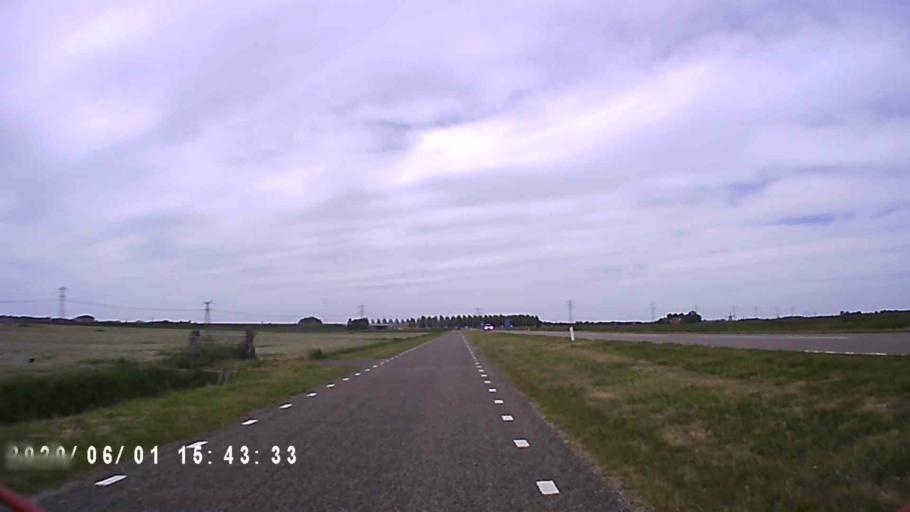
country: NL
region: Friesland
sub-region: Gemeente Boarnsterhim
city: Wergea
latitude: 53.1612
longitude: 5.8280
